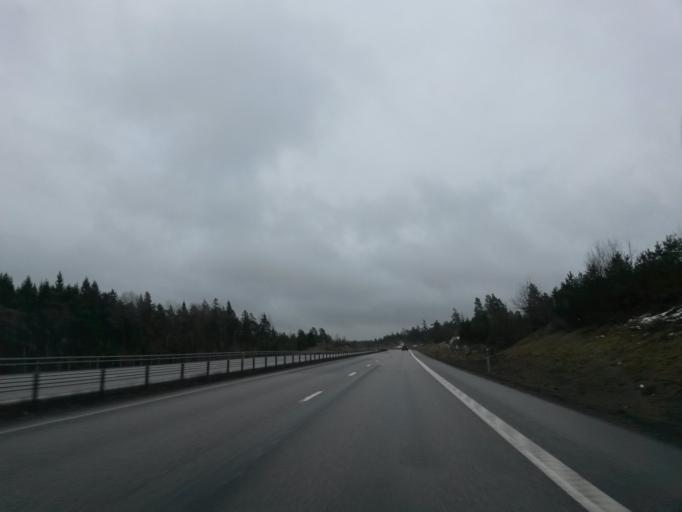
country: SE
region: Vaestra Goetaland
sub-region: Uddevalla Kommun
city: Uddevalla
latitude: 58.3308
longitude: 12.0218
